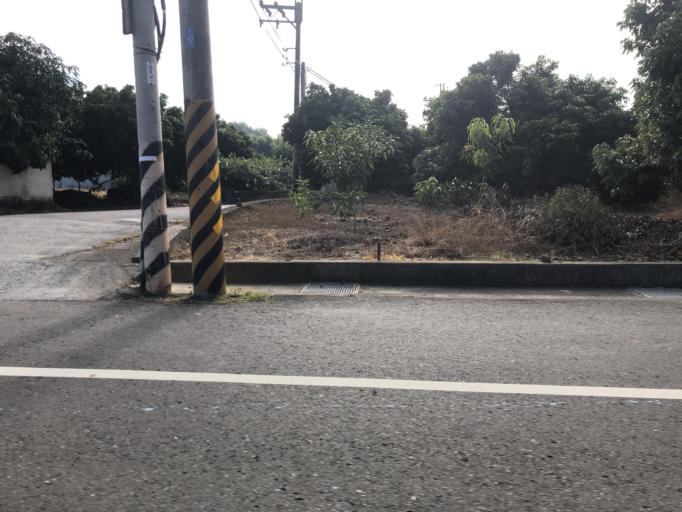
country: TW
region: Taiwan
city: Yujing
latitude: 23.0506
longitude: 120.4203
